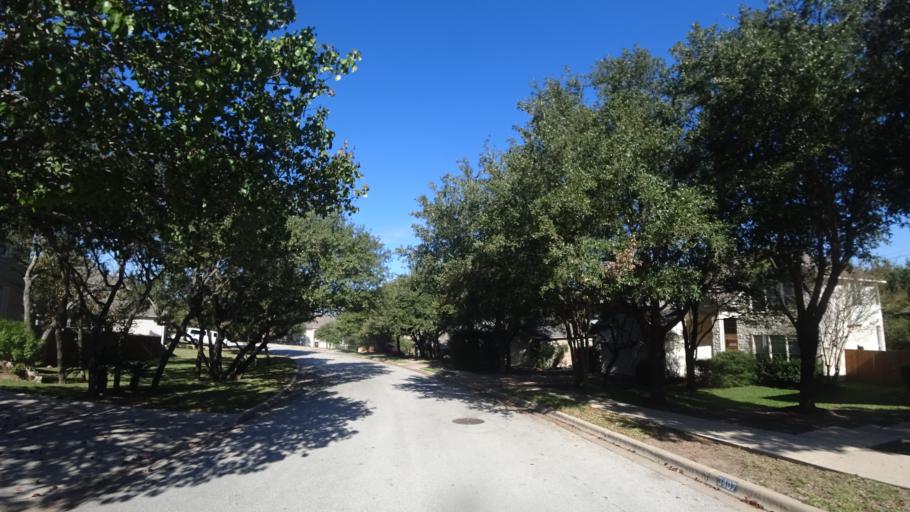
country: US
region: Texas
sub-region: Travis County
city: Hudson Bend
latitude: 30.3772
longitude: -97.8957
